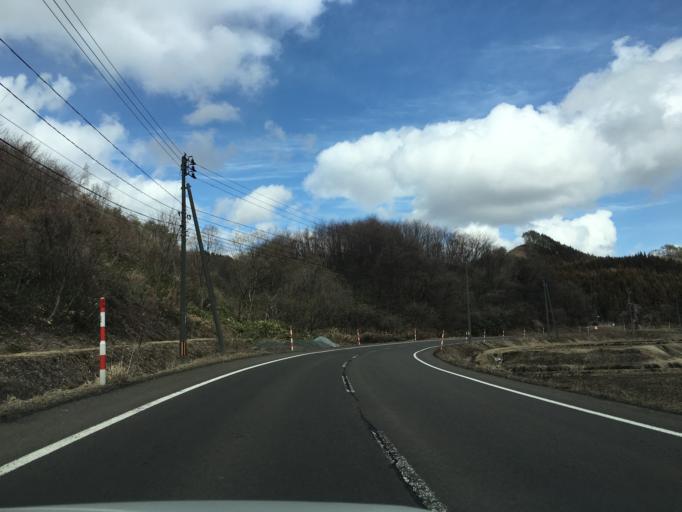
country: JP
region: Akita
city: Odate
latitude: 40.1848
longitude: 140.5008
